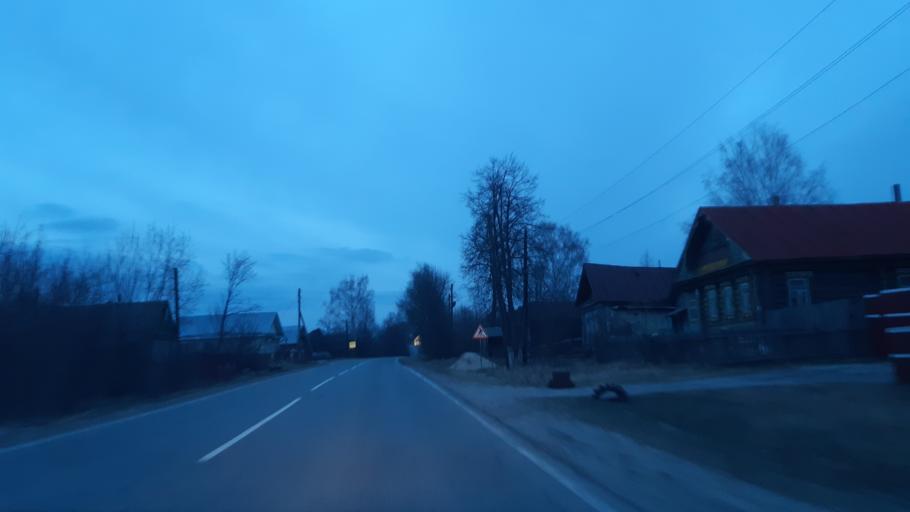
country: RU
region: Vladimir
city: Luknovo
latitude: 56.1877
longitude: 42.0202
